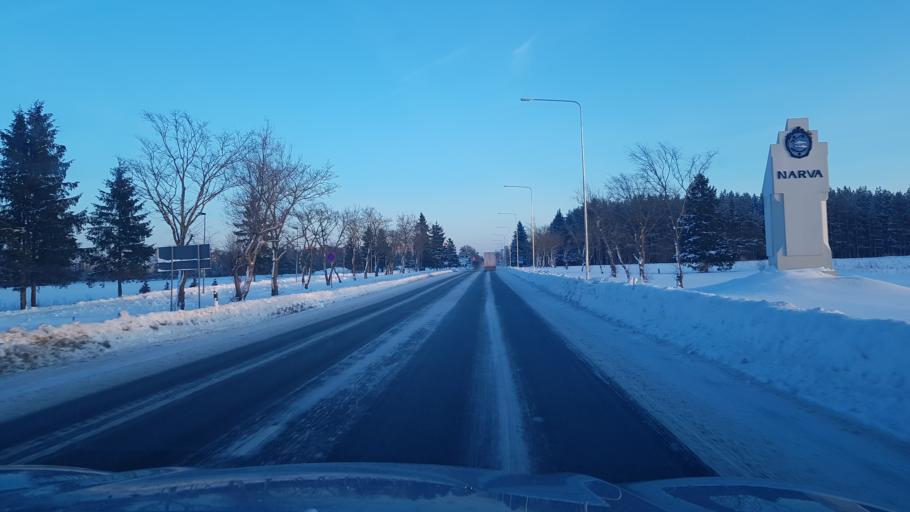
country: EE
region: Ida-Virumaa
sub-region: Narva linn
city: Narva
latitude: 59.3866
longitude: 28.1488
